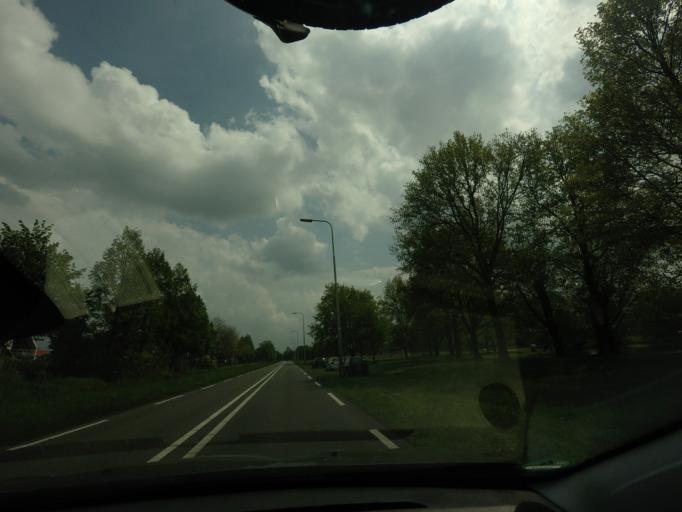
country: NL
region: Overijssel
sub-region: Gemeente Haaksbergen
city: Haaksbergen
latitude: 52.1505
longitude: 6.7324
